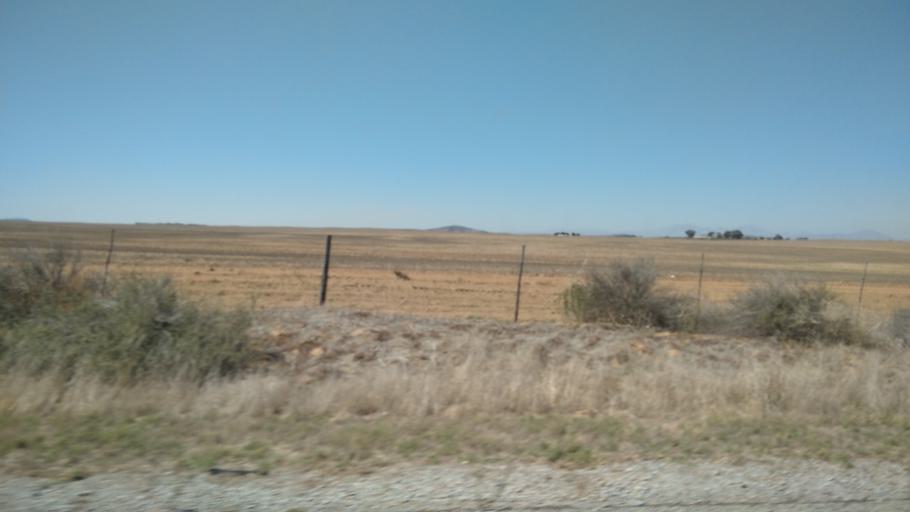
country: ZA
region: Western Cape
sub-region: West Coast District Municipality
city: Moorreesburg
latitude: -33.2408
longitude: 18.5711
